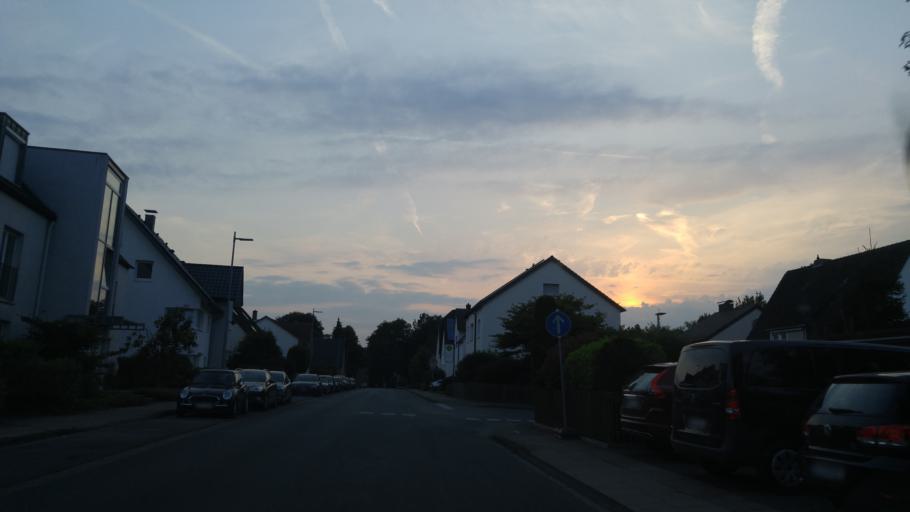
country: DE
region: North Rhine-Westphalia
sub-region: Regierungsbezirk Detmold
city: Bielefeld
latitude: 52.0555
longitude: 8.5405
